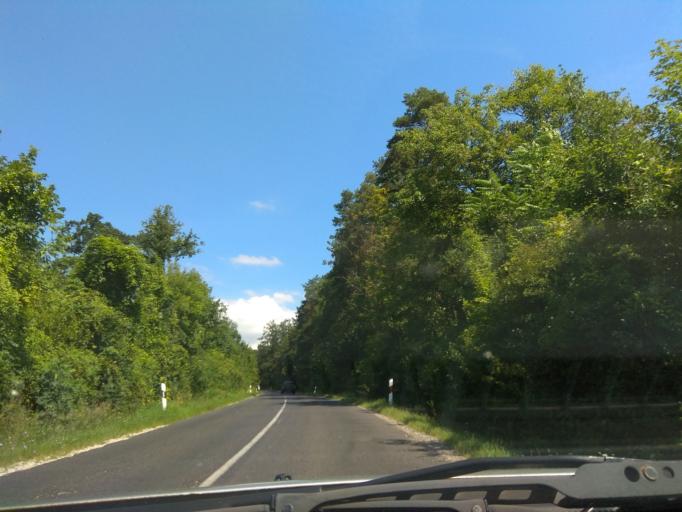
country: HU
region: Borsod-Abauj-Zemplen
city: Harsany
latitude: 48.0163
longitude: 20.7642
